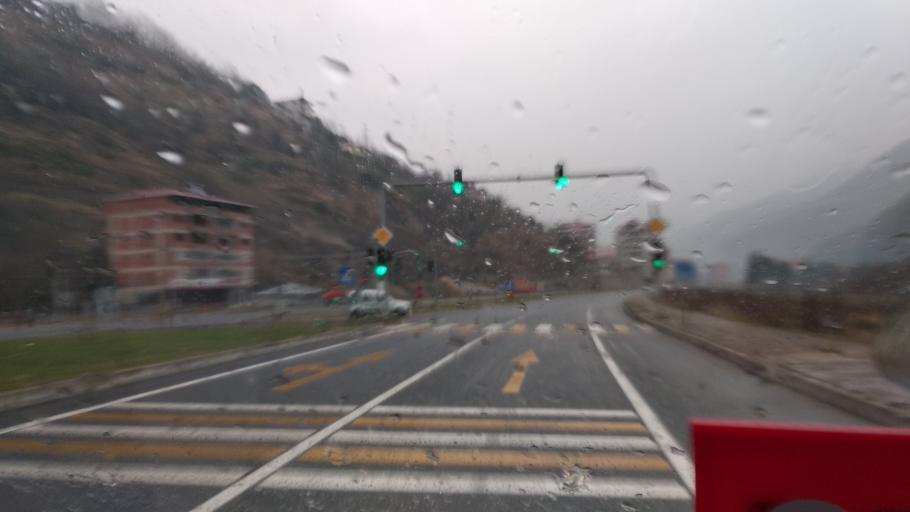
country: TR
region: Trabzon
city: Esiroglu
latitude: 40.8746
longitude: 39.6858
